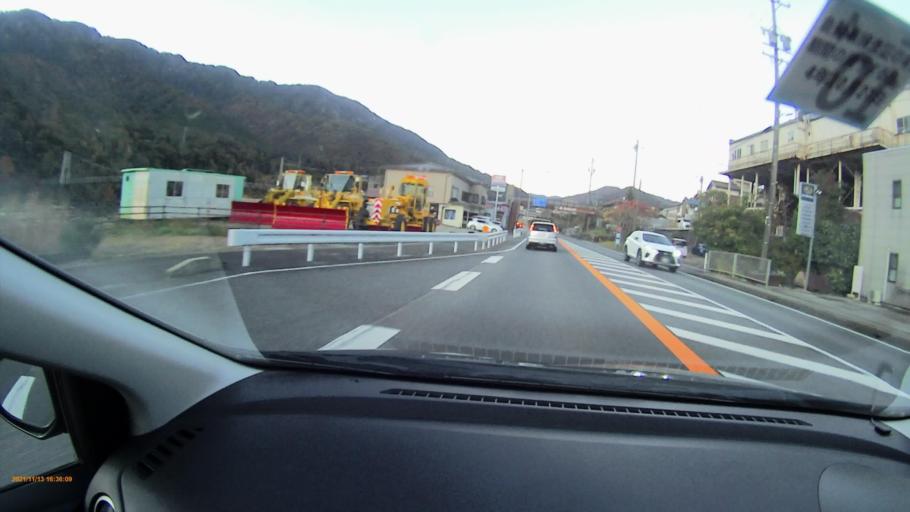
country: JP
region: Gifu
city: Nakatsugawa
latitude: 35.5993
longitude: 137.6074
